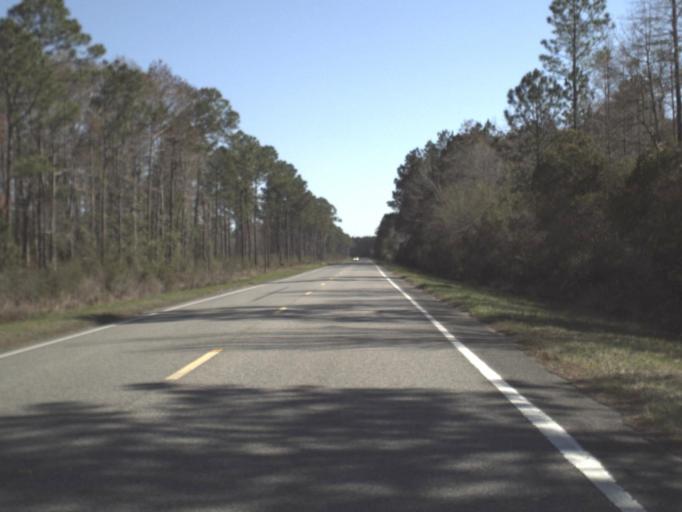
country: US
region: Florida
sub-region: Leon County
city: Woodville
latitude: 30.3209
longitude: -84.0371
